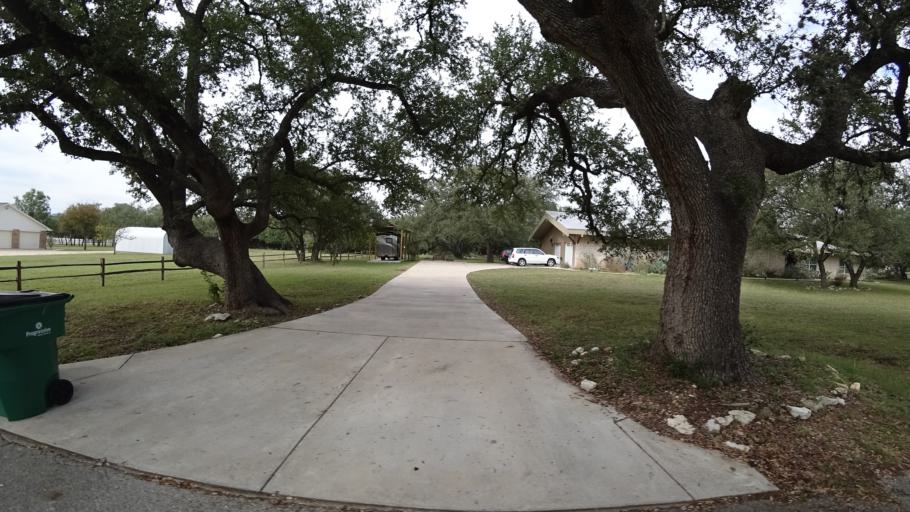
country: US
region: Texas
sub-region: Travis County
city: Shady Hollow
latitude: 30.2107
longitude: -97.8968
